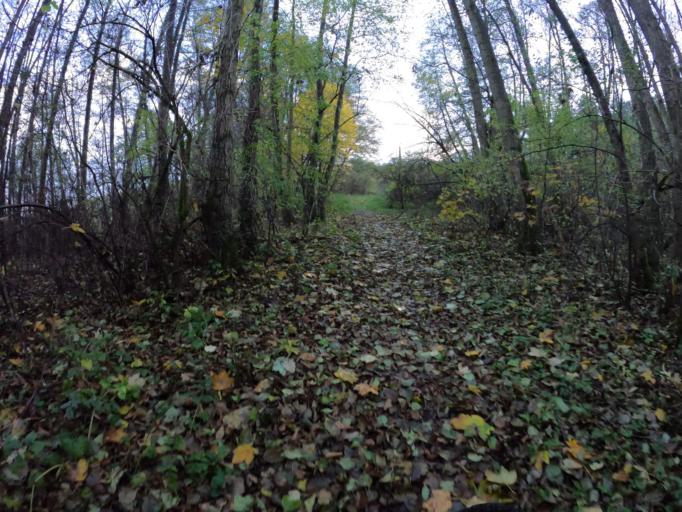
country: PL
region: West Pomeranian Voivodeship
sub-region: Powiat walecki
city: Tuczno
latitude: 53.1857
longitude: 16.1697
